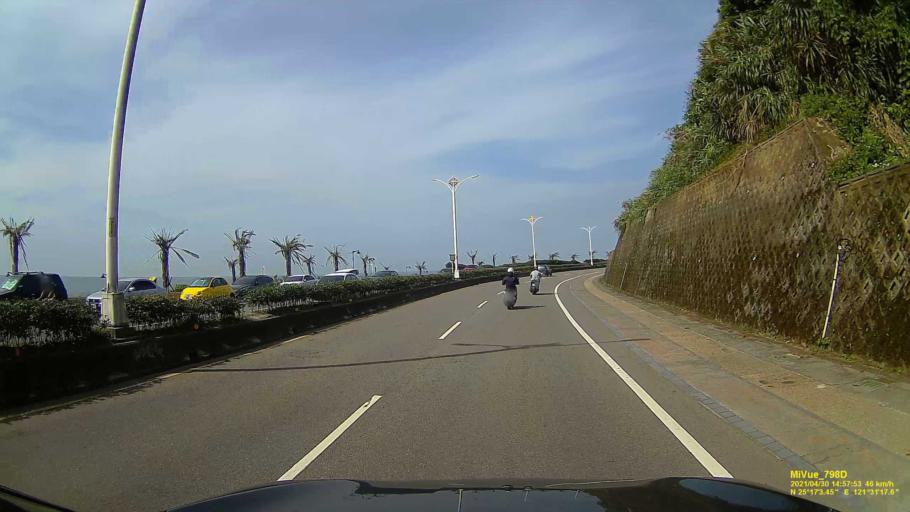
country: TW
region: Taipei
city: Taipei
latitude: 25.2845
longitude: 121.5218
